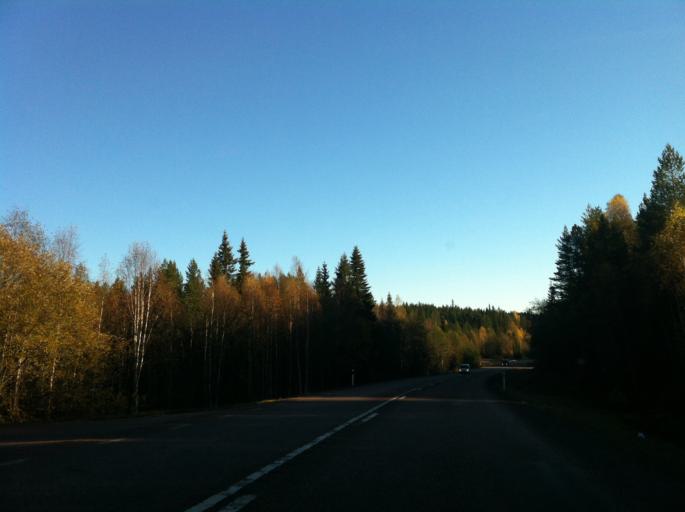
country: SE
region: Dalarna
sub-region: Faluns Kommun
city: Bjursas
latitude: 60.7820
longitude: 15.3119
